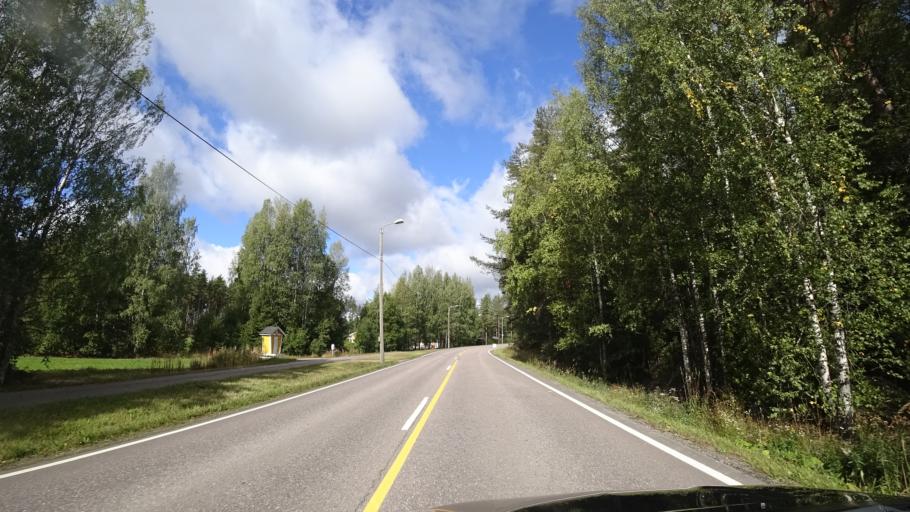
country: FI
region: Uusimaa
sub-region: Helsinki
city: Hyvinge
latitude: 60.6589
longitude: 24.9839
